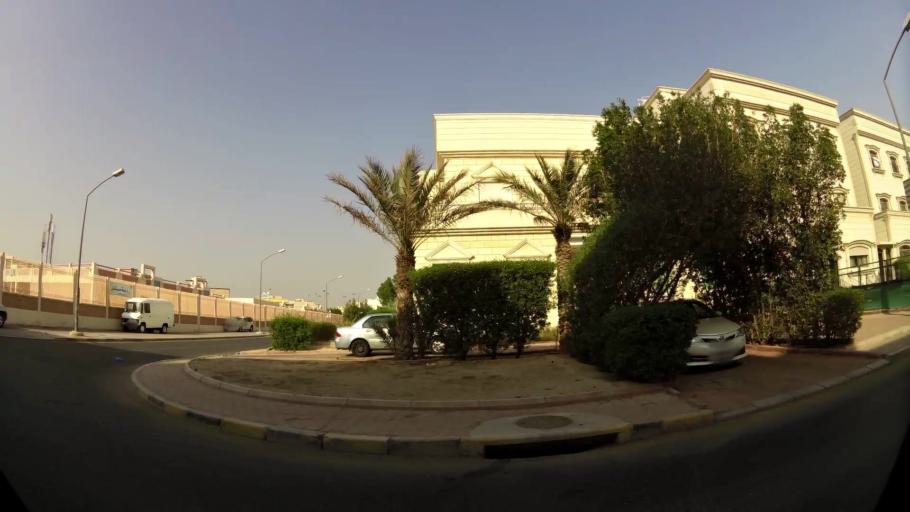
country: KW
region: Muhafazat al Jahra'
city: Al Jahra'
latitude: 29.3039
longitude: 47.7909
